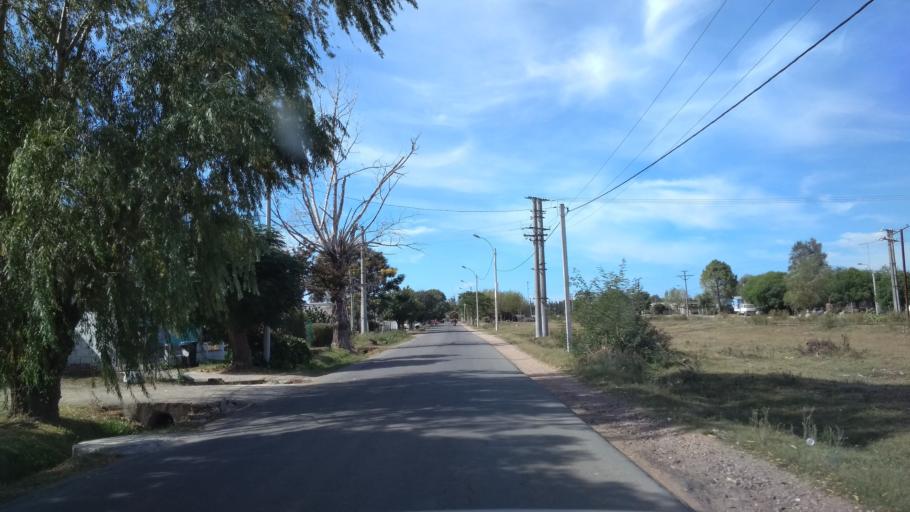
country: UY
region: Canelones
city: San Ramon
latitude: -34.2934
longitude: -55.9605
